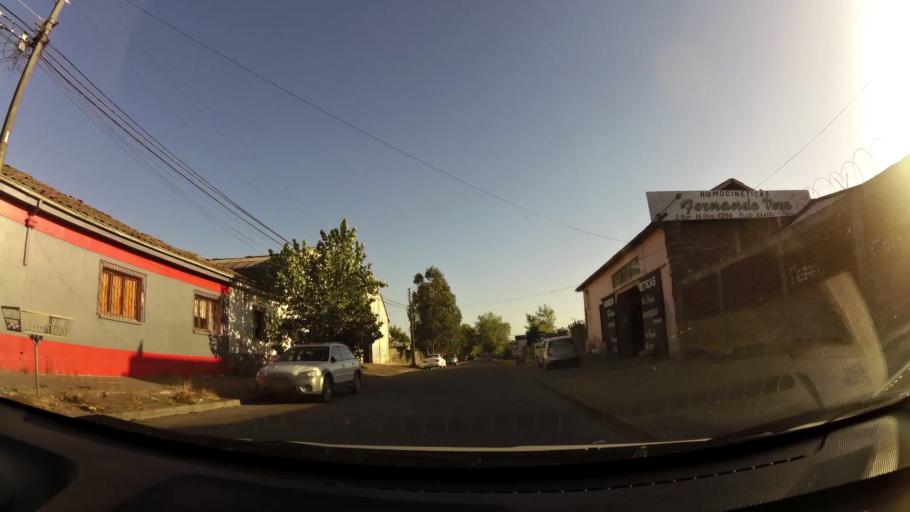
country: CL
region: Maule
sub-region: Provincia de Talca
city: Talca
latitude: -35.4302
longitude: -71.6432
